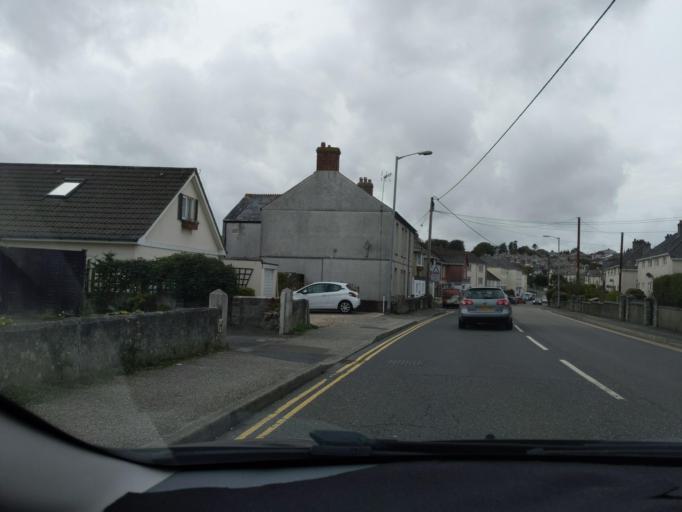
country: GB
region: England
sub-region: Cornwall
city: St Austell
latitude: 50.3414
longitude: -4.7770
